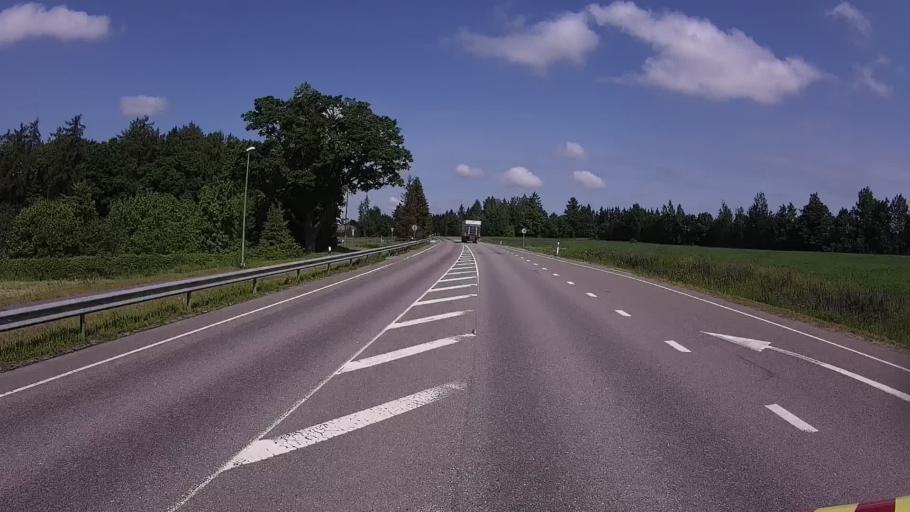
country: EE
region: Tartu
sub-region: UElenurme vald
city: Ulenurme
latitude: 58.2505
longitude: 26.7851
